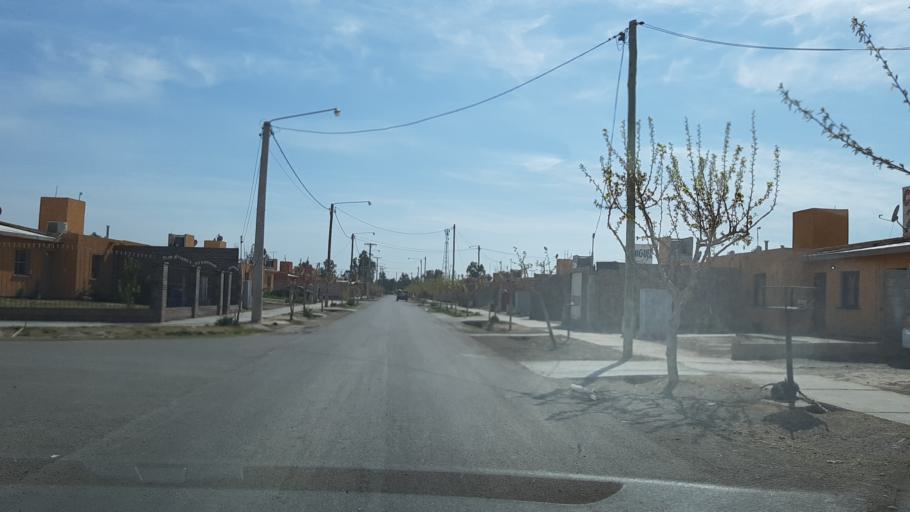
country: AR
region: San Juan
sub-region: Departamento de Zonda
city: Zonda
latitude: -31.5469
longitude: -68.7397
